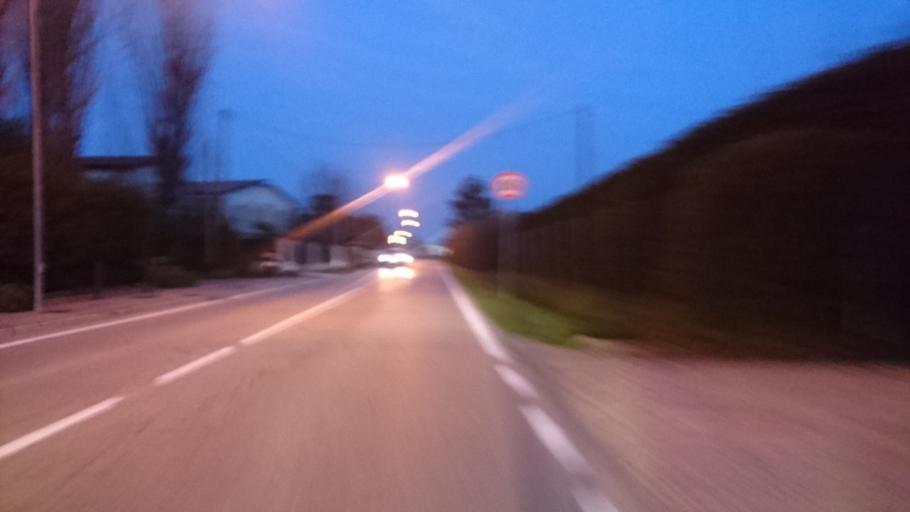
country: IT
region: Veneto
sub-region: Provincia di Padova
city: Selvazzano Dentro
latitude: 45.3726
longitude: 11.7924
